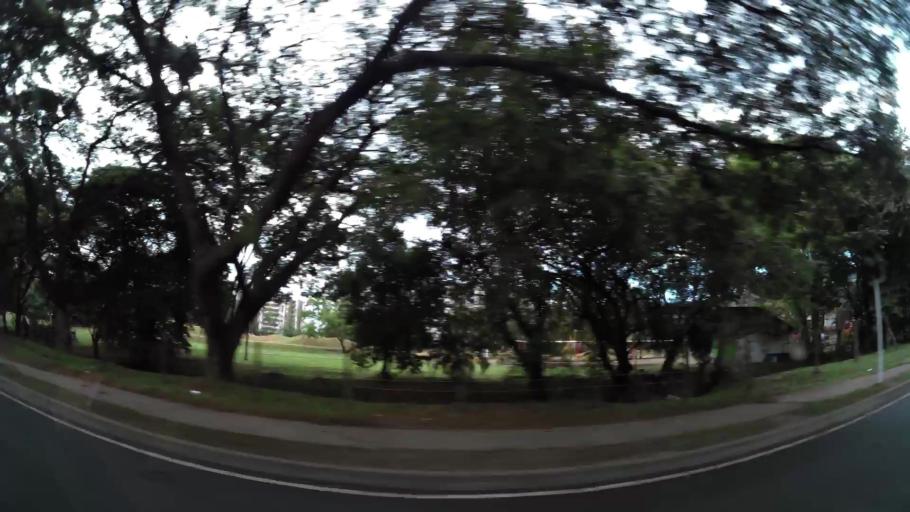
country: CO
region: Valle del Cauca
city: Cali
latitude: 3.4937
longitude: -76.5205
